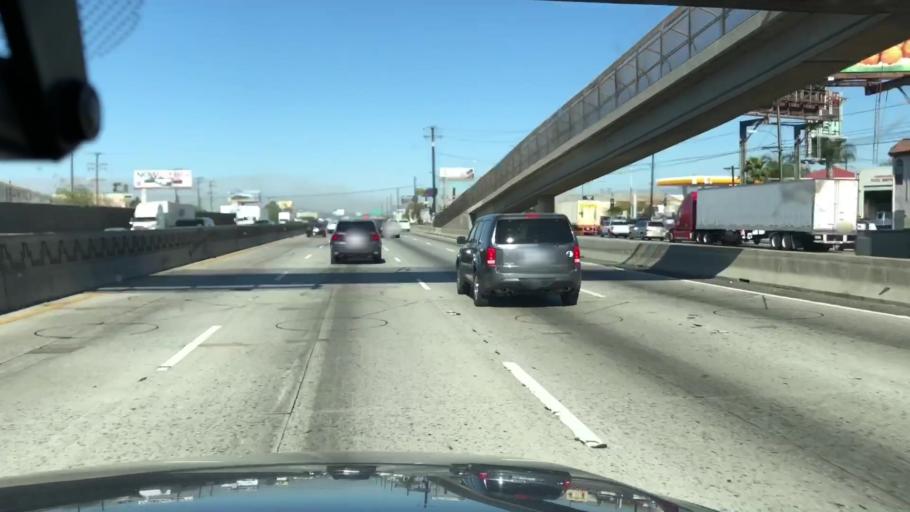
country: US
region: California
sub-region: Los Angeles County
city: Bell Gardens
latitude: 33.9787
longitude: -118.1276
